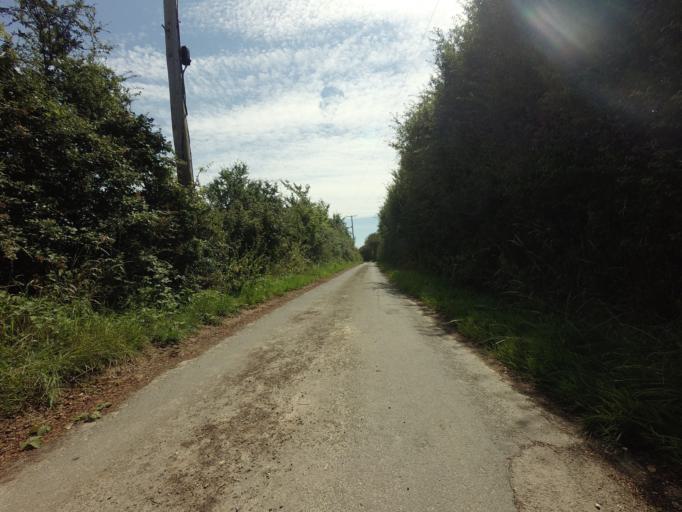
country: GB
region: England
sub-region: Kent
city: Stone
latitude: 50.9916
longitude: 0.8342
